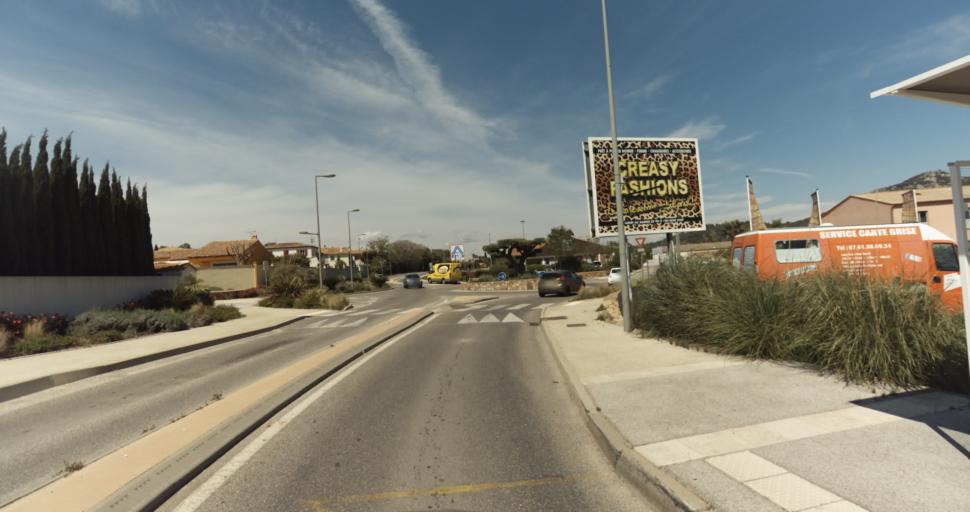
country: FR
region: Provence-Alpes-Cote d'Azur
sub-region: Departement du Var
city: La Crau
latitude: 43.1242
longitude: 6.0732
